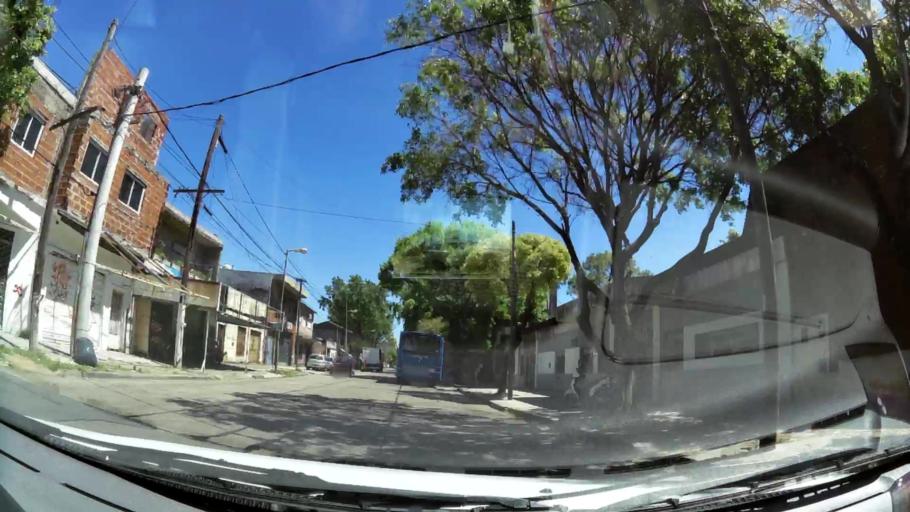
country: AR
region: Buenos Aires
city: Caseros
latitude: -34.5859
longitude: -58.5531
